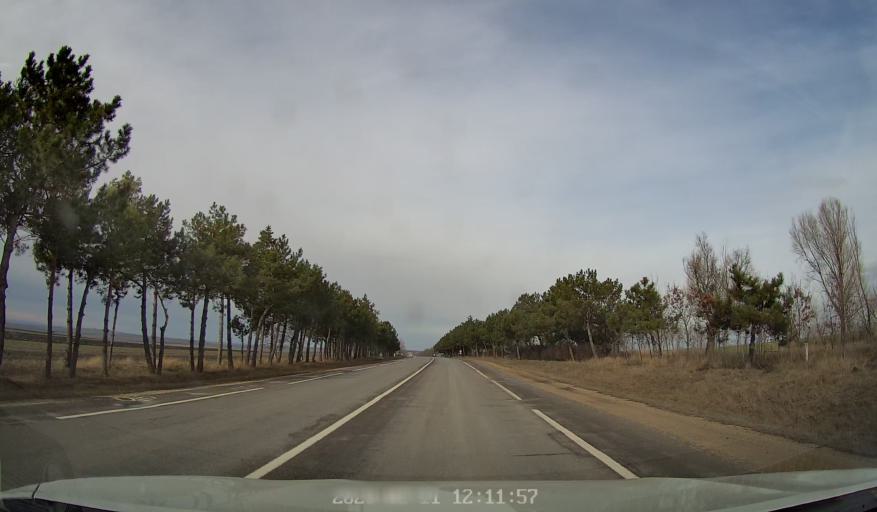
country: MD
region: Riscani
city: Riscani
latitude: 48.0583
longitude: 27.5102
